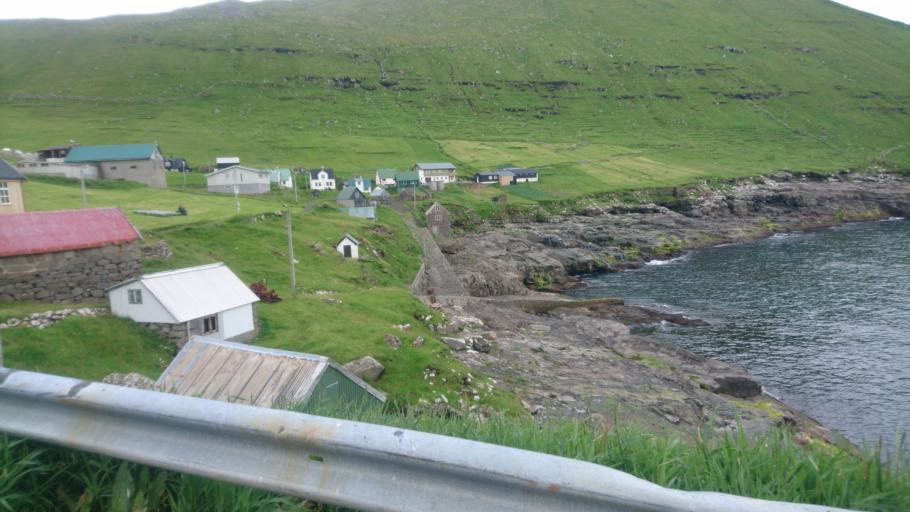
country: FO
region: Nordoyar
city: Klaksvik
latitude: 62.3286
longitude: -6.2767
